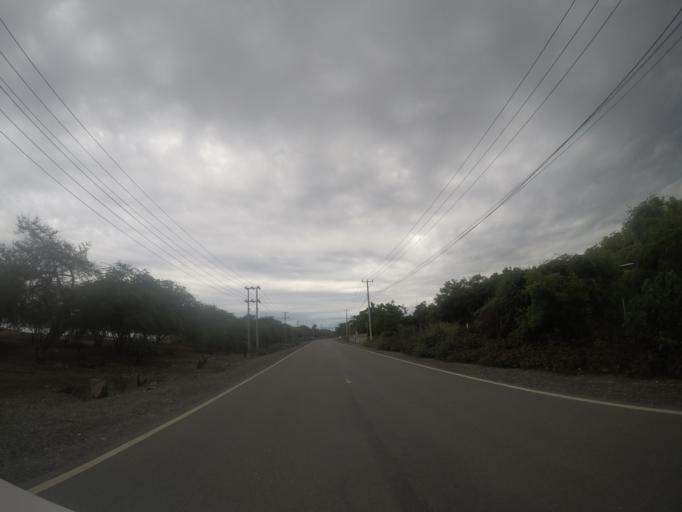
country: TL
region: Liquica
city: Liquica
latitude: -8.5660
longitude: 125.3905
